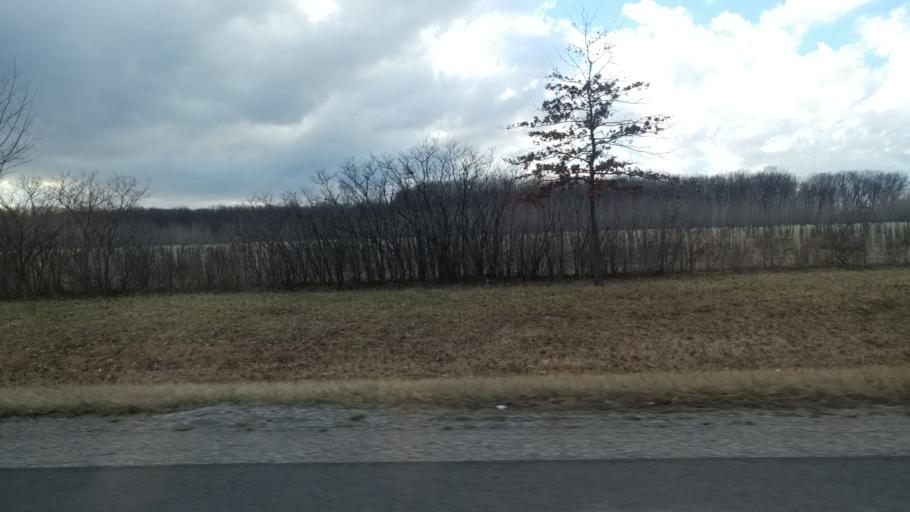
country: US
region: Ohio
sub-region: Lucas County
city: Maumee
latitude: 41.5531
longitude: -83.6886
